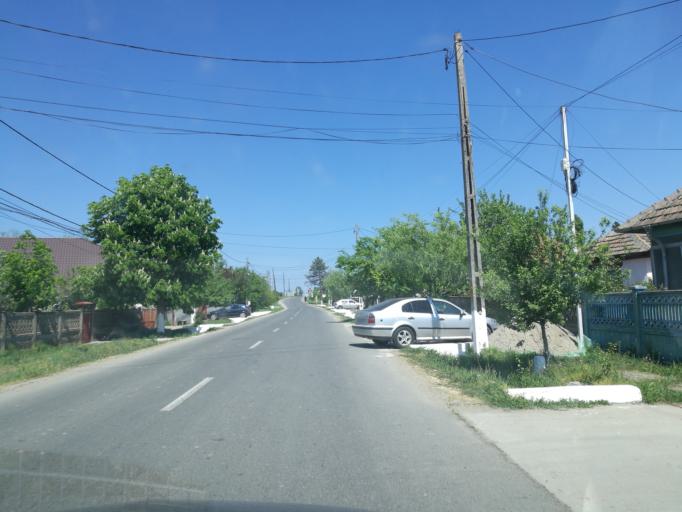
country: RO
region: Ialomita
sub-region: Comuna Adancata
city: Adancata
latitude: 44.7717
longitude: 26.4328
